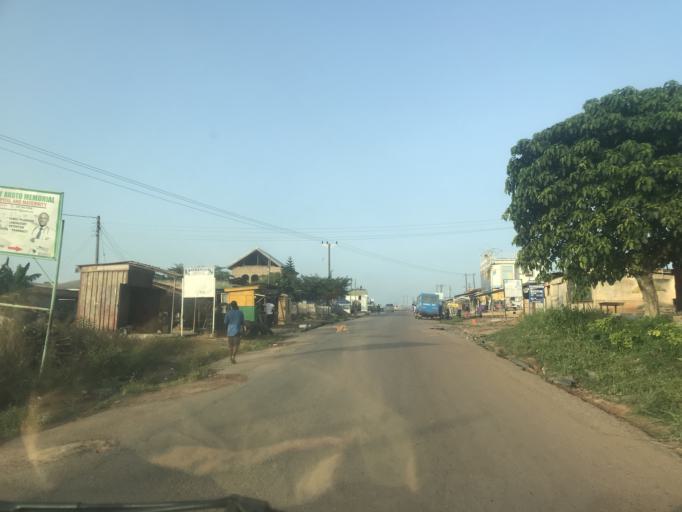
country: GH
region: Ashanti
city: Obuasi
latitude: 6.2034
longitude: -1.6059
